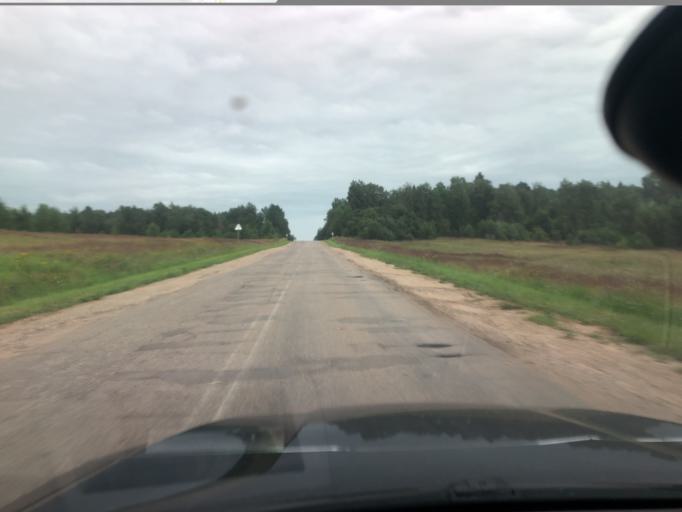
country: RU
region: Jaroslavl
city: Petrovsk
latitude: 56.9853
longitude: 39.1497
